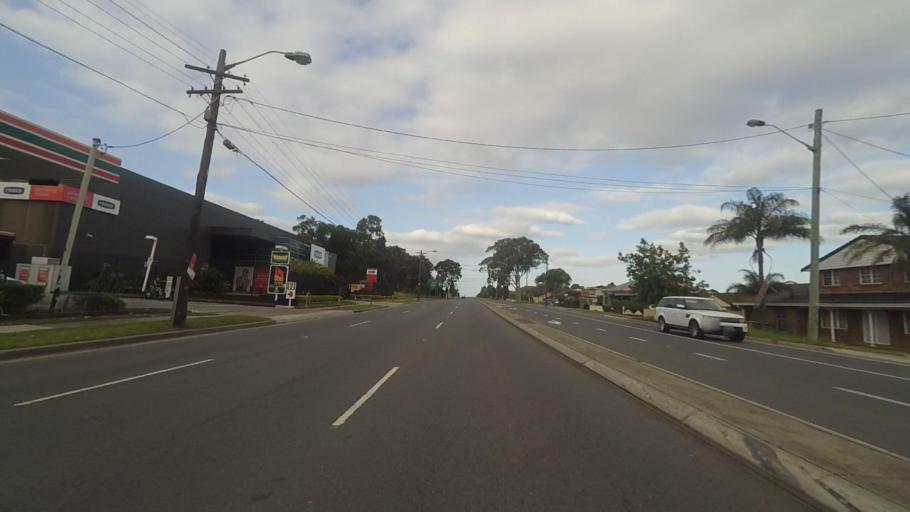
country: AU
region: New South Wales
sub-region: Bankstown
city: Revesby
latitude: -33.9372
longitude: 151.0211
